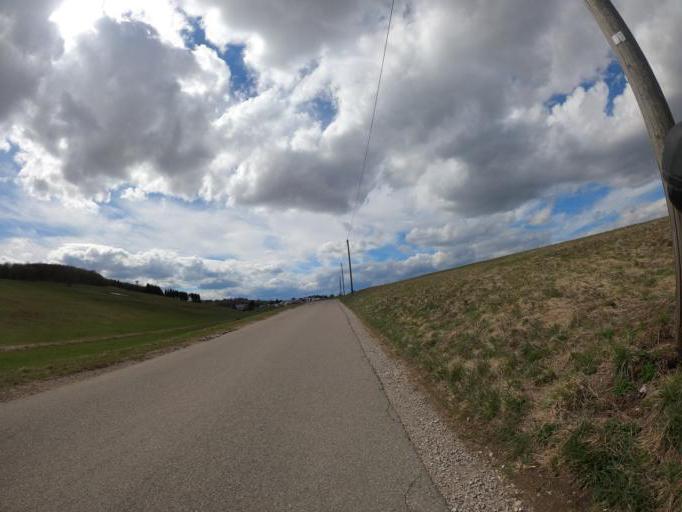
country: DE
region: Baden-Wuerttemberg
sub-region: Tuebingen Region
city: Pfullingen
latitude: 48.3868
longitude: 9.2012
